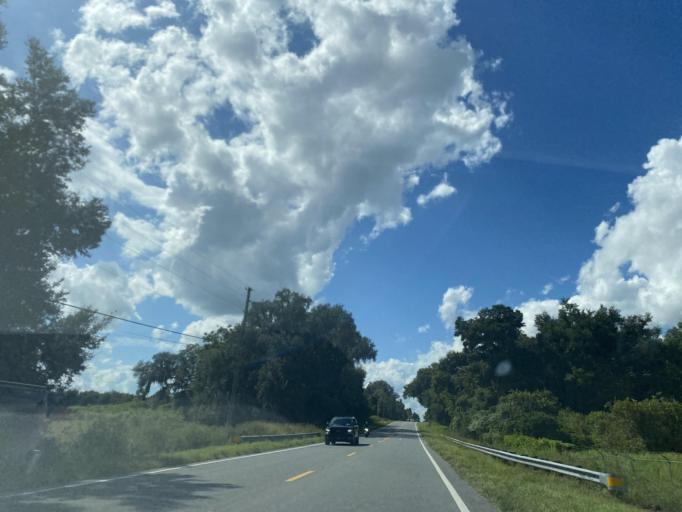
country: US
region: Florida
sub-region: Sumter County
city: The Villages
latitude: 28.9819
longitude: -81.9430
